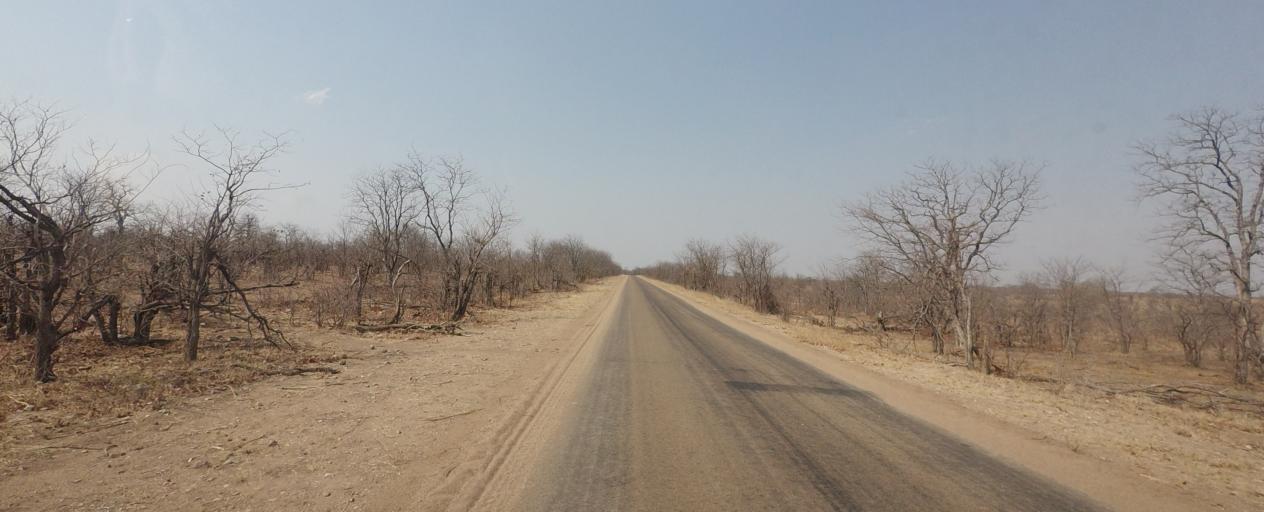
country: ZA
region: Limpopo
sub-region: Mopani District Municipality
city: Giyani
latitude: -23.1951
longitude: 31.3122
